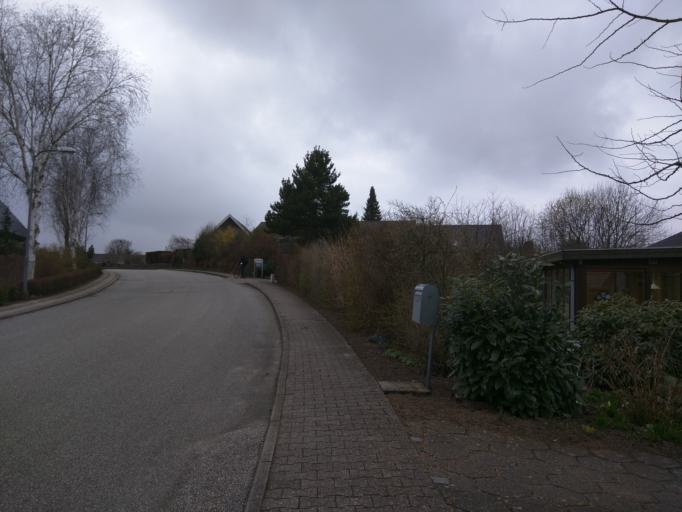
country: DK
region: South Denmark
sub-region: Fredericia Kommune
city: Snoghoj
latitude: 55.5410
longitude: 9.7136
